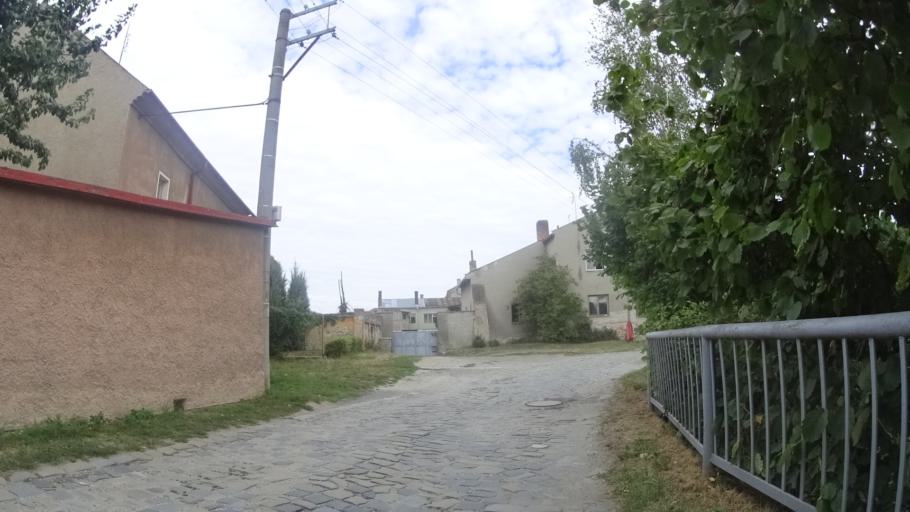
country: CZ
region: Olomoucky
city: Tovacov
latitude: 49.4288
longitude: 17.2898
